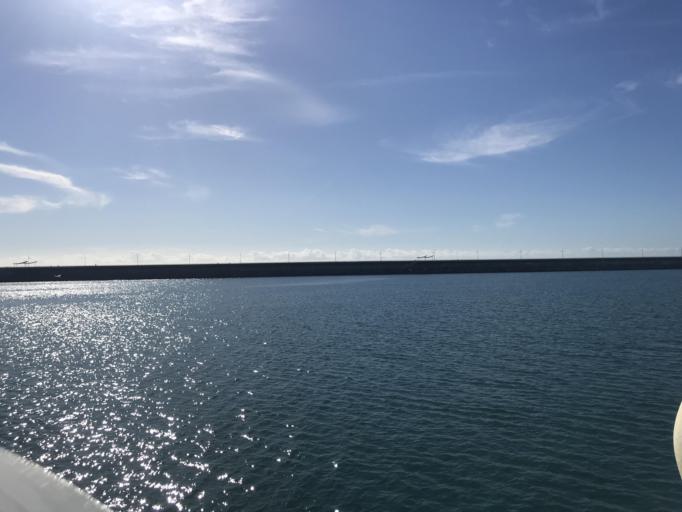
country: ES
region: Valencia
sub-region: Provincia de Alicante
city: Torrevieja
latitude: 37.9694
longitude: -0.6862
